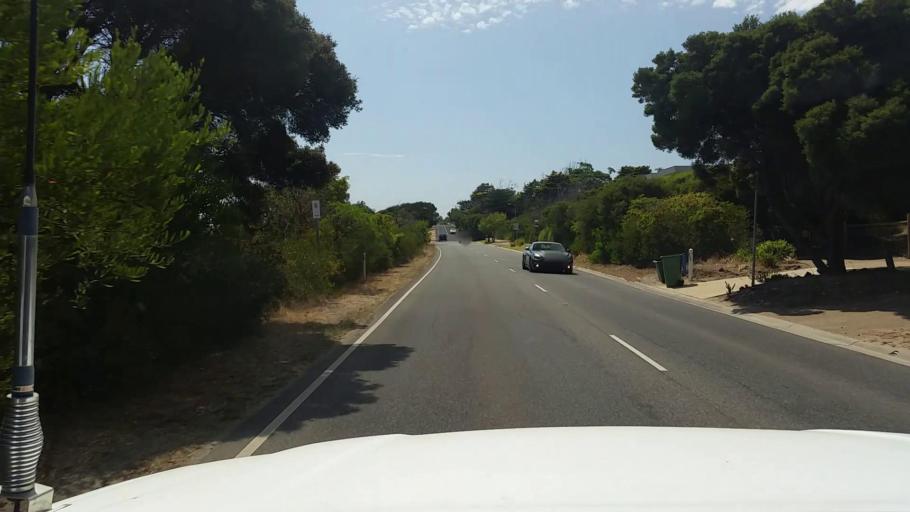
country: AU
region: Victoria
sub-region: Mornington Peninsula
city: Mount Martha
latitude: -38.2608
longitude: 145.0198
